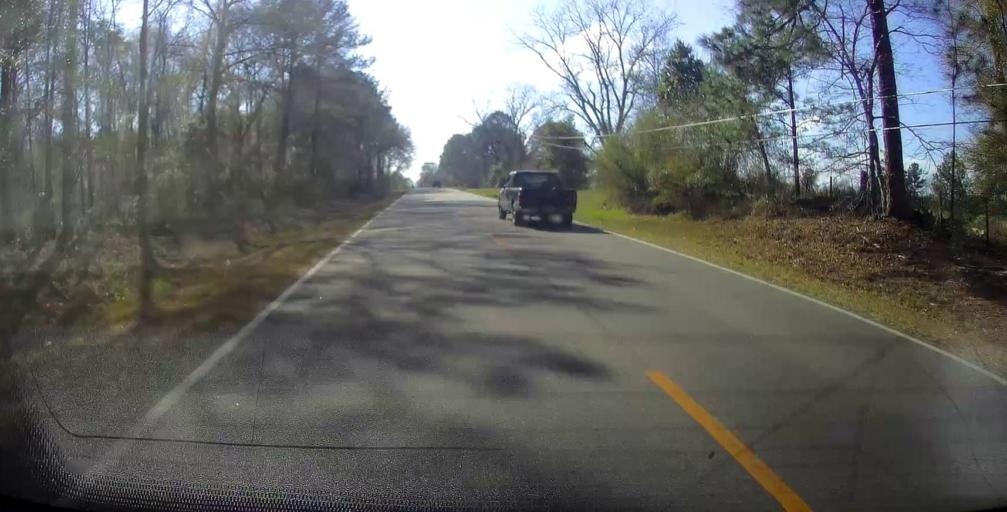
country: US
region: Georgia
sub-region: Laurens County
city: Dublin
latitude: 32.5361
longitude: -82.9641
